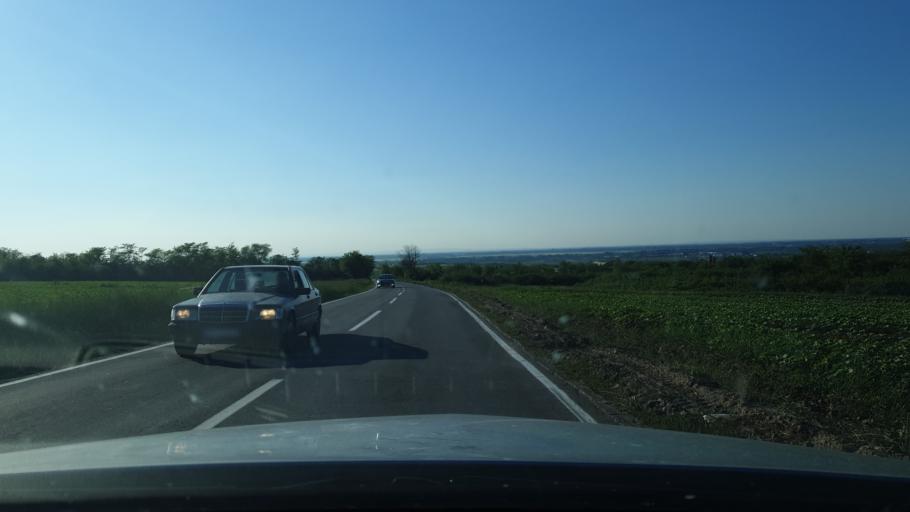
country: RS
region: Central Serbia
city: Sremcica
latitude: 44.7031
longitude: 20.3743
